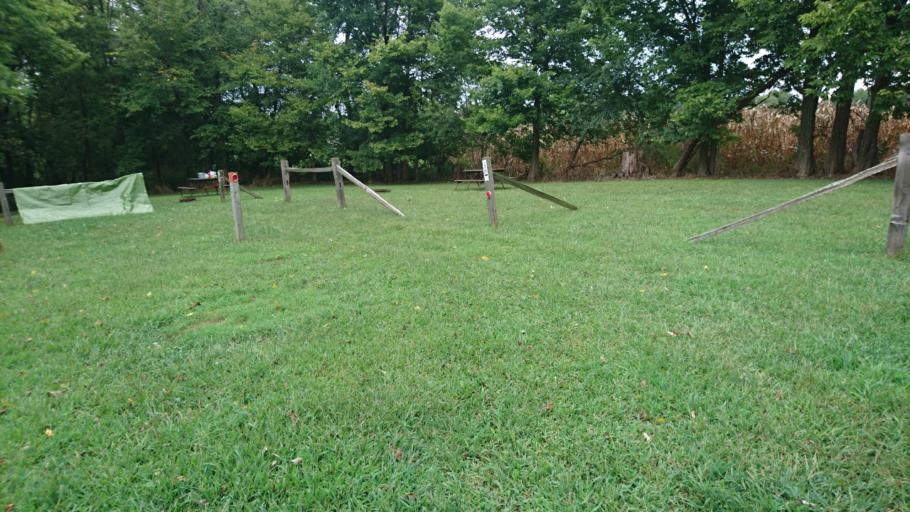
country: US
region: Illinois
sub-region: Sangamon County
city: Chatham
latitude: 39.6587
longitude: -89.6518
